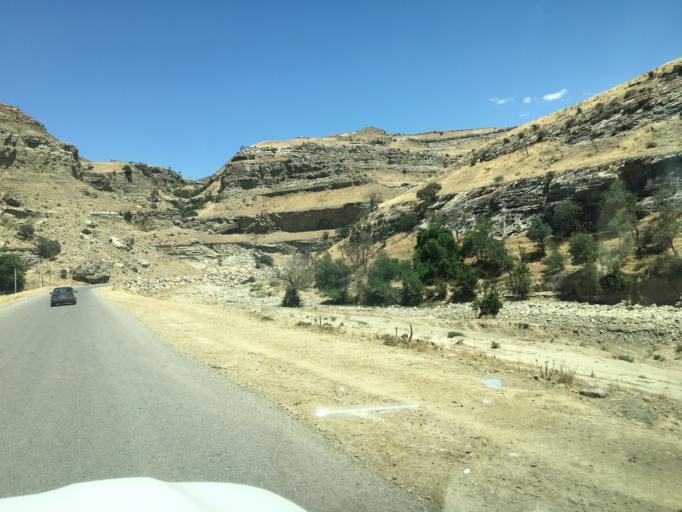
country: TM
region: Balkan
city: Magtymguly
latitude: 38.4196
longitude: 56.6865
